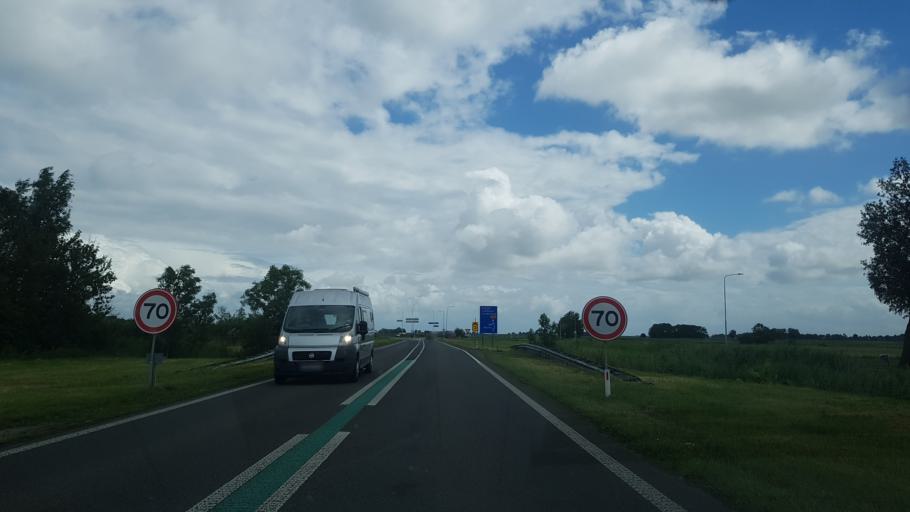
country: NL
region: Friesland
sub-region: Gemeente Dongeradeel
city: Anjum
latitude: 53.3685
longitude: 6.0893
